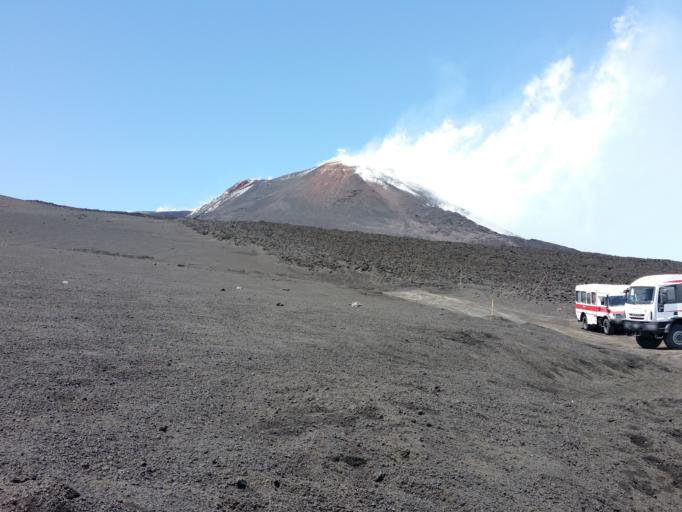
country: IT
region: Sicily
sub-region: Catania
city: Milo
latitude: 37.7325
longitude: 15.0071
